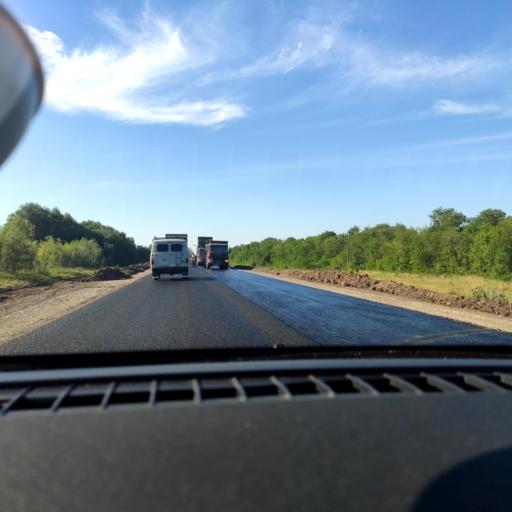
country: RU
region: Samara
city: Krasnoarmeyskoye
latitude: 52.8101
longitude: 50.0120
